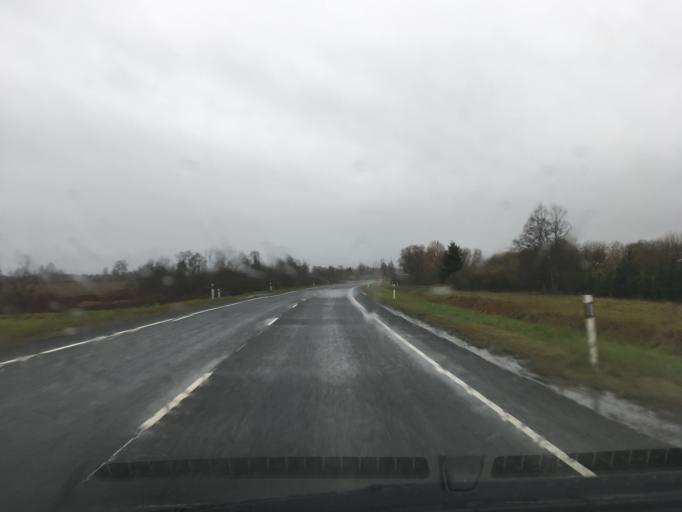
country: EE
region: Harju
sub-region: Nissi vald
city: Turba
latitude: 58.9218
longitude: 24.1126
